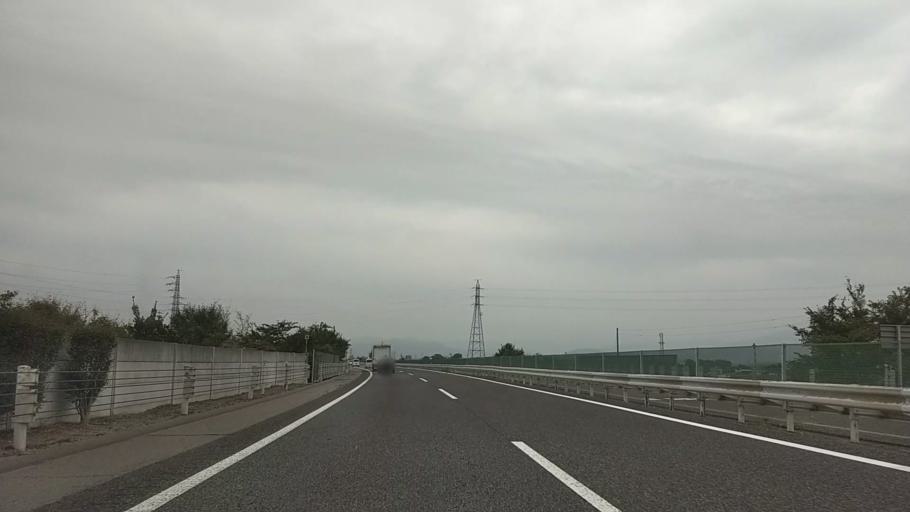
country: JP
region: Nagano
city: Matsumoto
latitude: 36.2088
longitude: 137.9297
